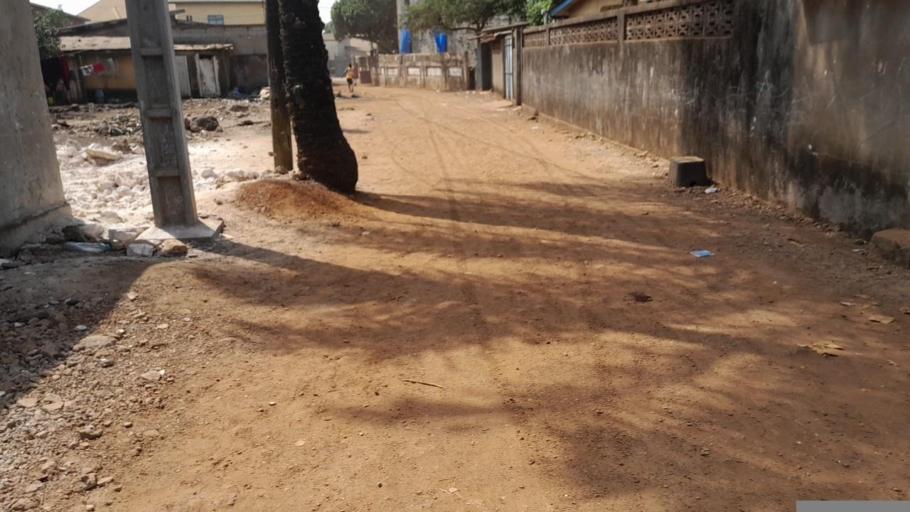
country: GN
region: Conakry
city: Conakry
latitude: 9.6112
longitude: -13.6156
